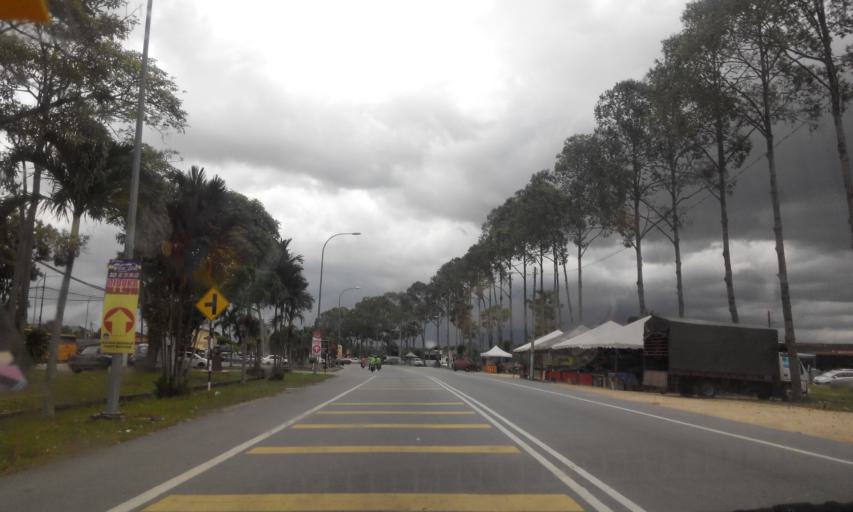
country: MY
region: Perak
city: Parit Buntar
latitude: 5.1119
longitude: 100.4883
